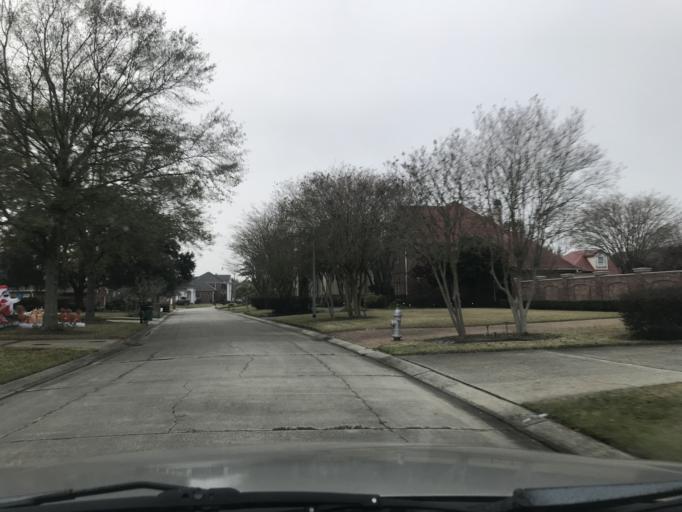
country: US
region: Louisiana
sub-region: Jefferson Parish
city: Woodmere
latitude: 29.8681
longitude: -90.0919
